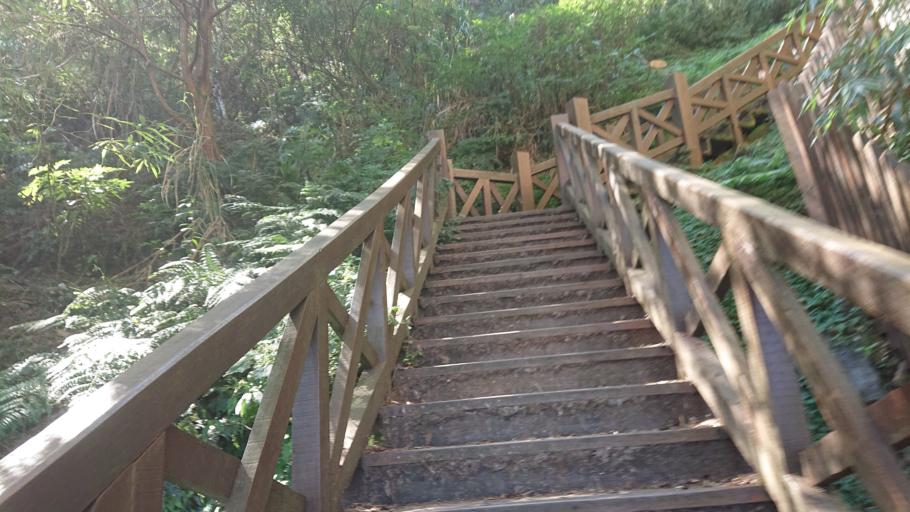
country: TW
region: Taiwan
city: Lugu
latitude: 23.4817
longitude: 120.8557
